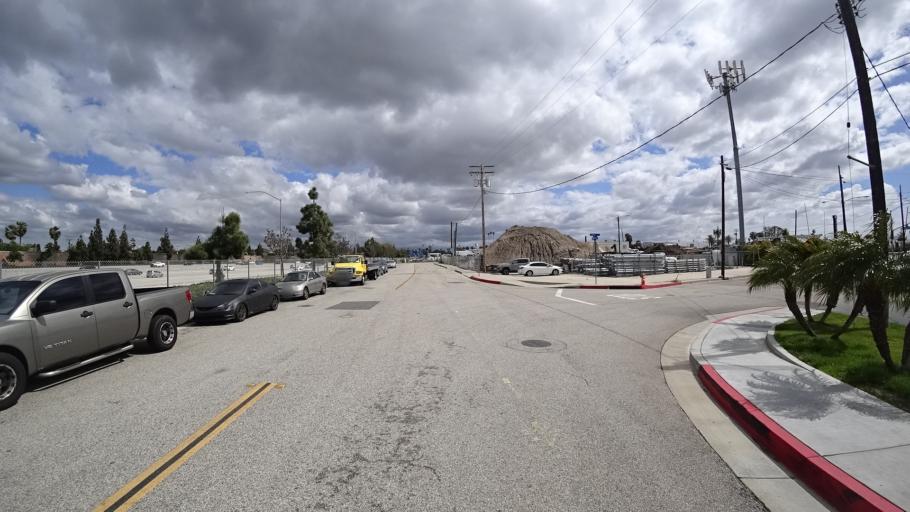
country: US
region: California
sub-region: Orange County
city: Anaheim
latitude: 33.8337
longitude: -117.9373
